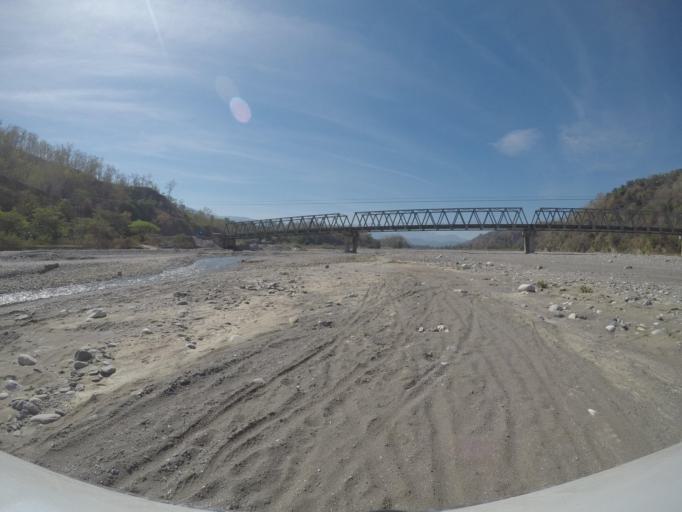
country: TL
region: Liquica
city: Maubara
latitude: -8.7888
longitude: 125.2569
